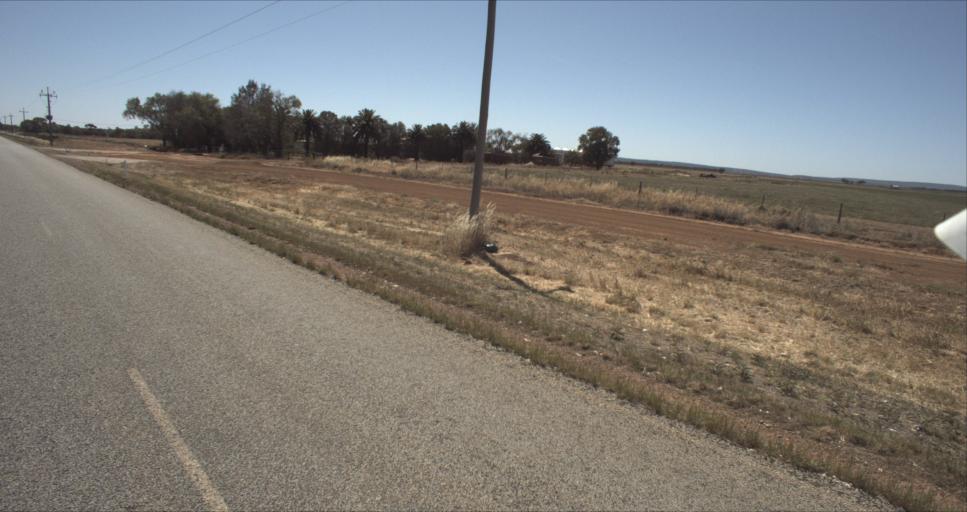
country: AU
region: New South Wales
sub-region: Leeton
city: Leeton
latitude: -34.4528
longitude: 146.2957
